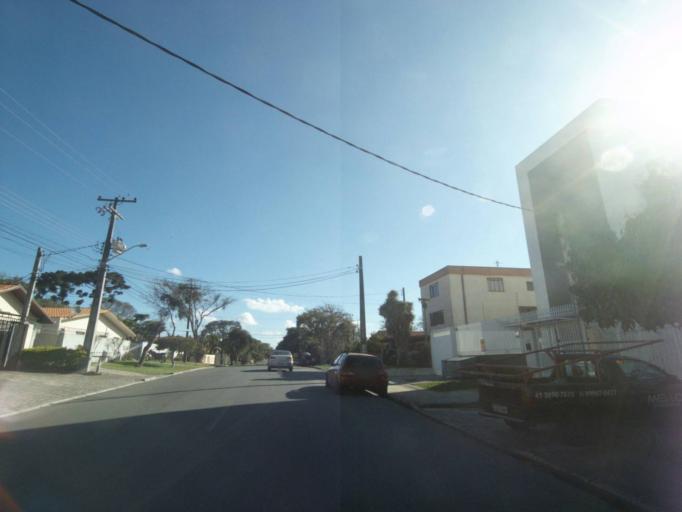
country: BR
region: Parana
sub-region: Curitiba
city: Curitiba
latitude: -25.3879
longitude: -49.2508
